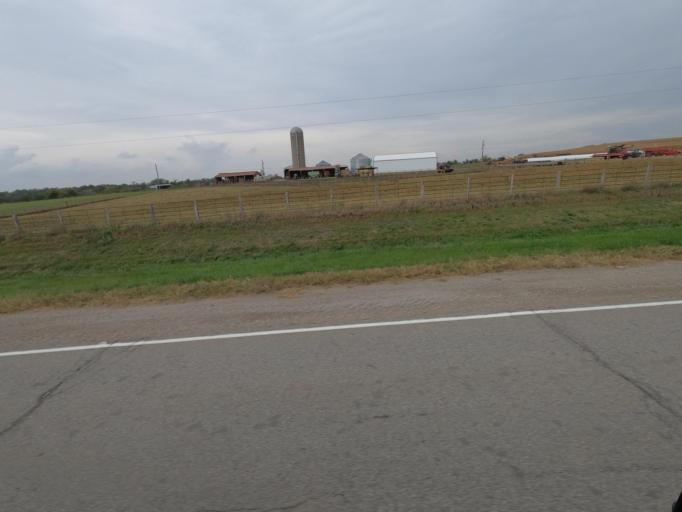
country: US
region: Iowa
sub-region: Van Buren County
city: Keosauqua
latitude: 40.8568
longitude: -92.0885
